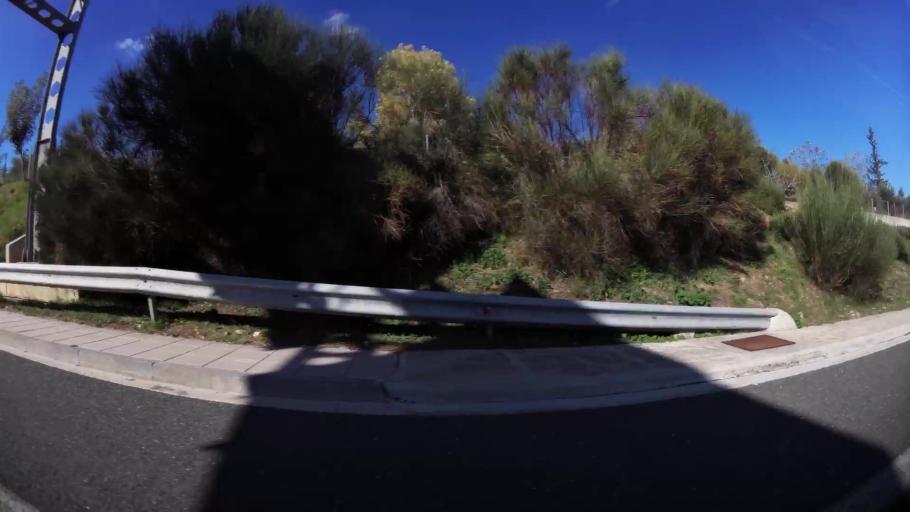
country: GR
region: Attica
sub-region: Nomarchia Anatolikis Attikis
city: Pallini
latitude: 37.9954
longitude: 23.8785
